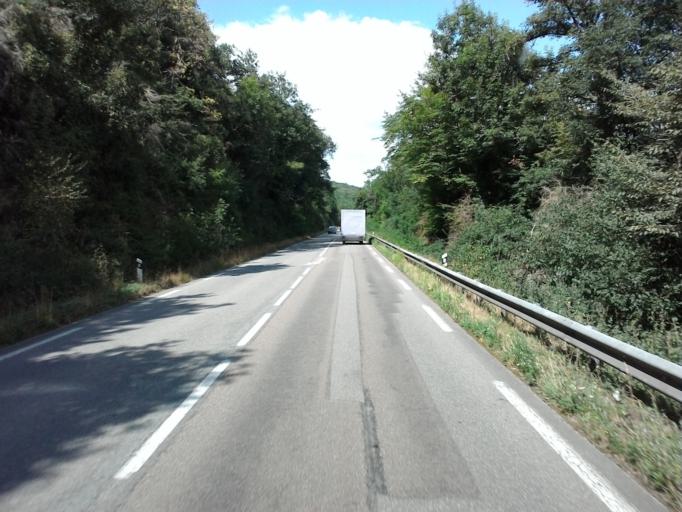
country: FR
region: Franche-Comte
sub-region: Departement du Doubs
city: Boussieres
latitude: 47.1456
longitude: 5.9342
